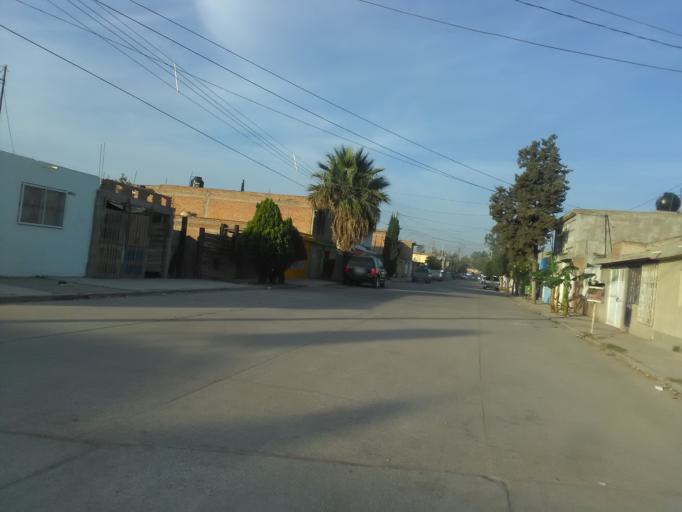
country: MX
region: Durango
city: Victoria de Durango
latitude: 24.0492
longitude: -104.6439
